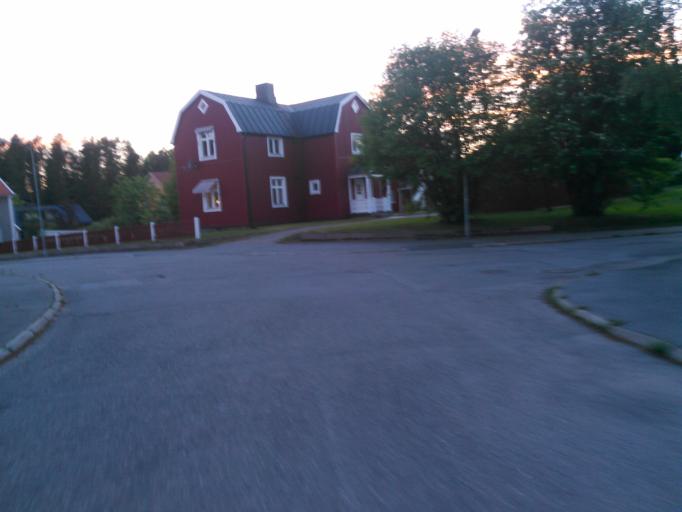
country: SE
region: Vaesterbotten
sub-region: Umea Kommun
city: Umea
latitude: 63.8114
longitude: 20.3007
